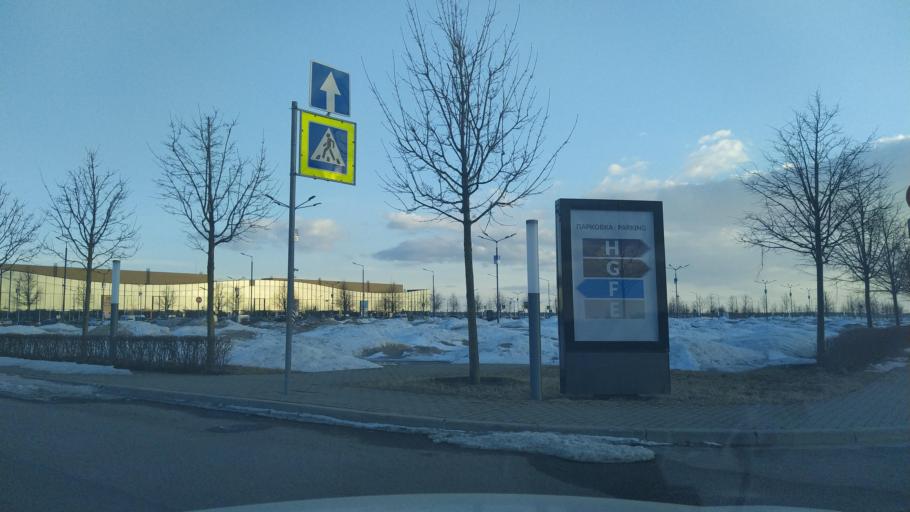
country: RU
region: St.-Petersburg
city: Aleksandrovskaya
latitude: 59.7627
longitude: 30.3502
